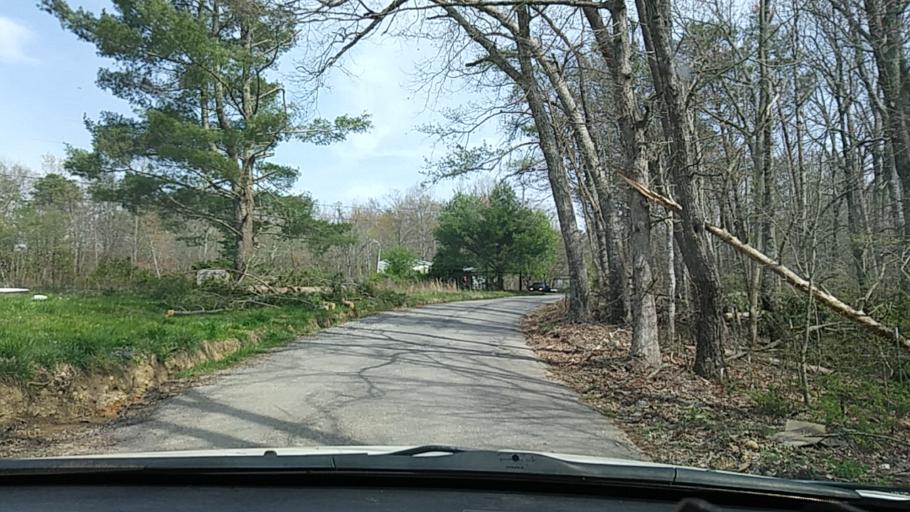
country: US
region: Tennessee
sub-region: Greene County
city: Tusculum
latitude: 36.0932
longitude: -82.6998
